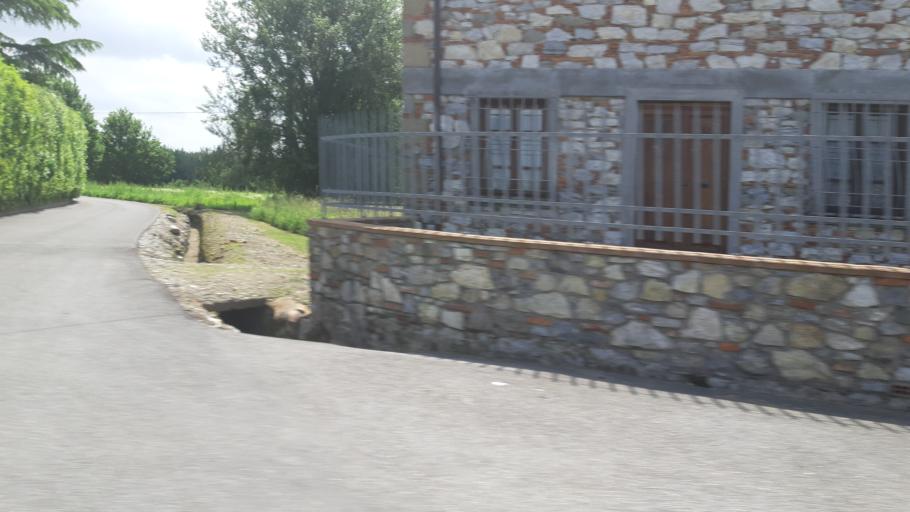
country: IT
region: Tuscany
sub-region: Provincia di Lucca
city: Capannori
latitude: 43.8682
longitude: 10.5722
